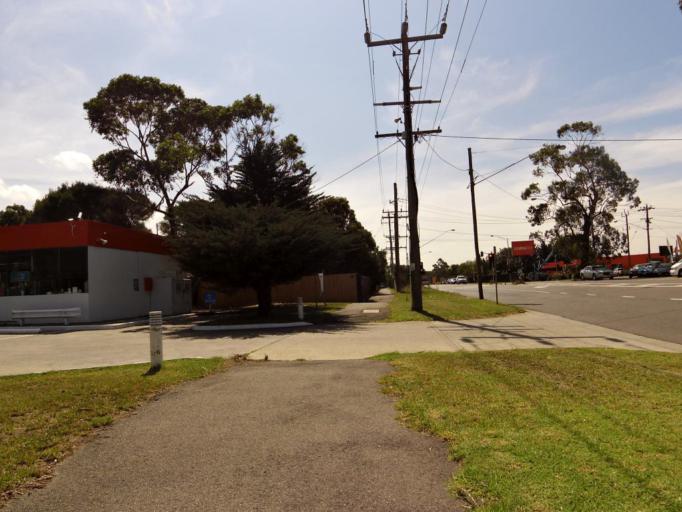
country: AU
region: Victoria
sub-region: Mornington Peninsula
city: Hastings
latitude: -38.2909
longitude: 145.1909
